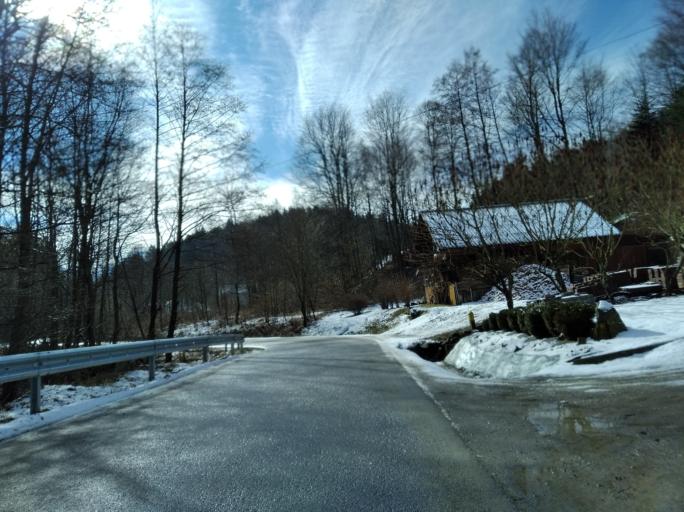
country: PL
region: Subcarpathian Voivodeship
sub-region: Powiat brzozowski
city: Jablonica Polska
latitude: 49.7488
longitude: 21.8804
